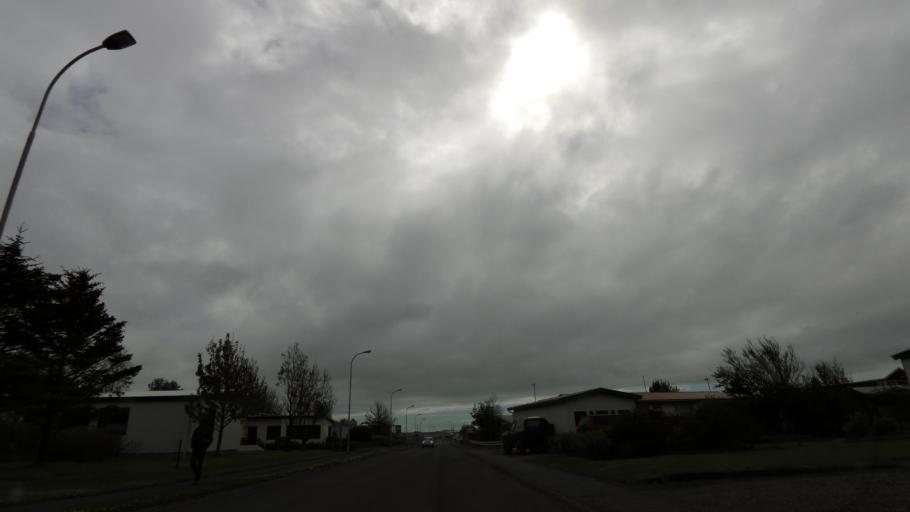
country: IS
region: East
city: Hoefn
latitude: 64.2563
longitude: -15.2117
